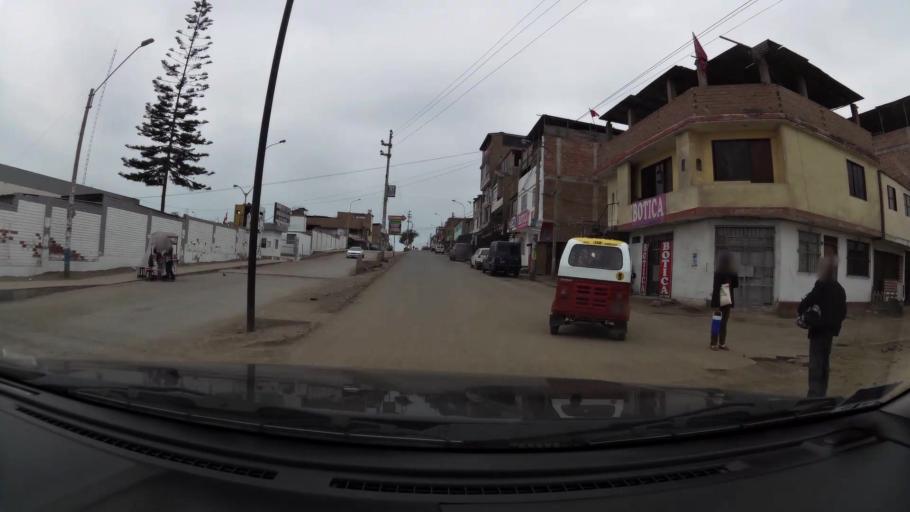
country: PE
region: Lima
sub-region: Lima
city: Surco
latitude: -12.1981
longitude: -76.9460
